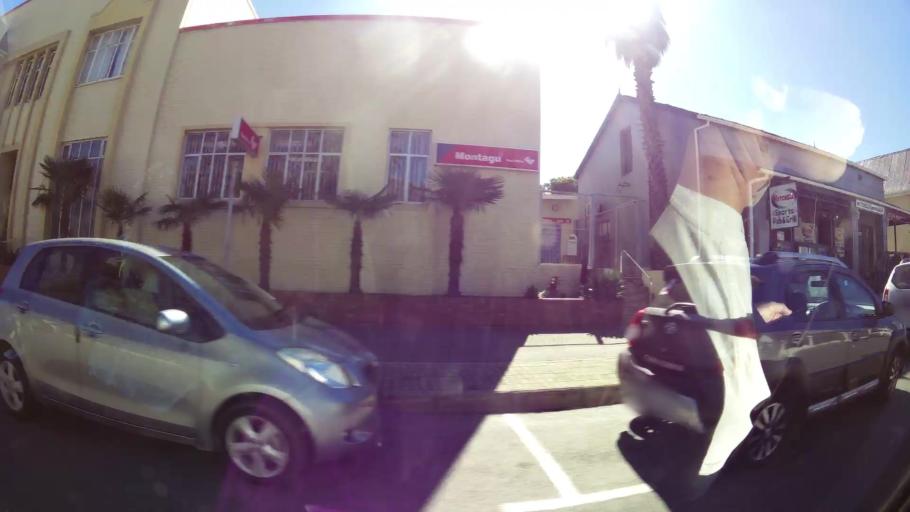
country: ZA
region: Western Cape
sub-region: Cape Winelands District Municipality
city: Ashton
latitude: -33.7870
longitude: 20.1201
